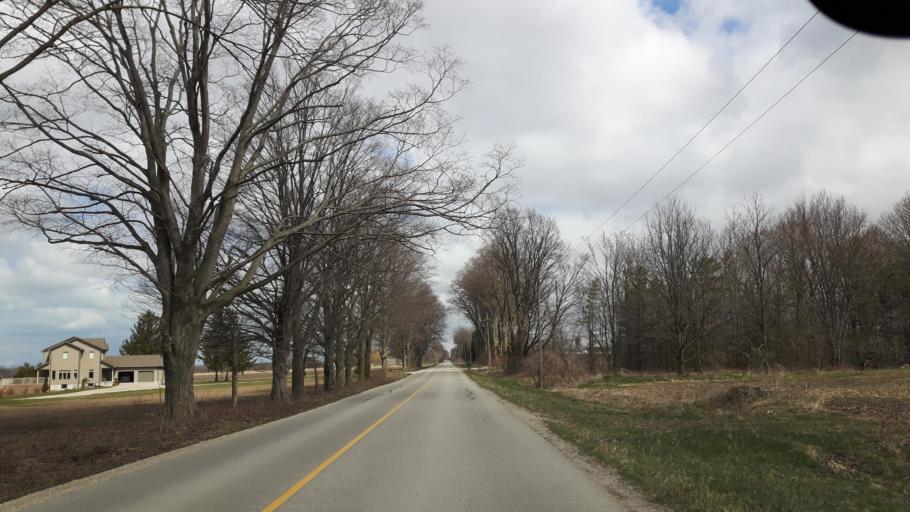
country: CA
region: Ontario
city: Goderich
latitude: 43.6923
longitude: -81.6848
